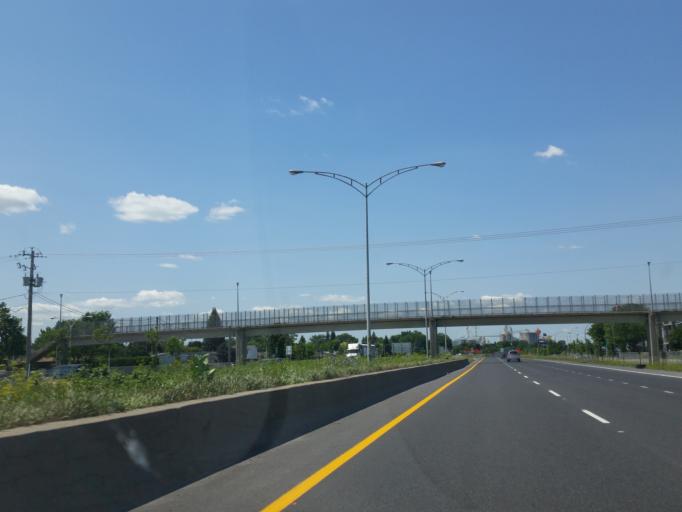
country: CA
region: Quebec
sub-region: Monteregie
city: Saint-Jean-sur-Richelieu
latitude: 45.3268
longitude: -73.2733
